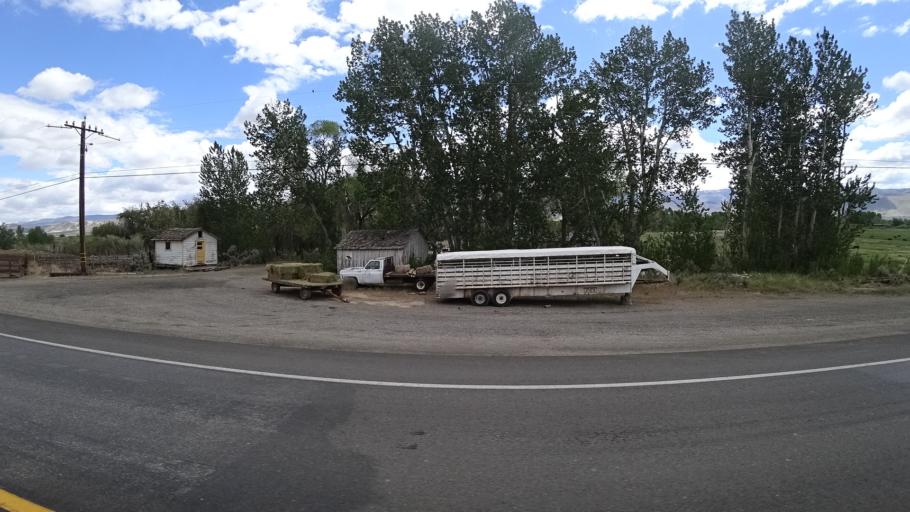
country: US
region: Nevada
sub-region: Lyon County
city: Smith Valley
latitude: 38.5537
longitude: -119.5026
